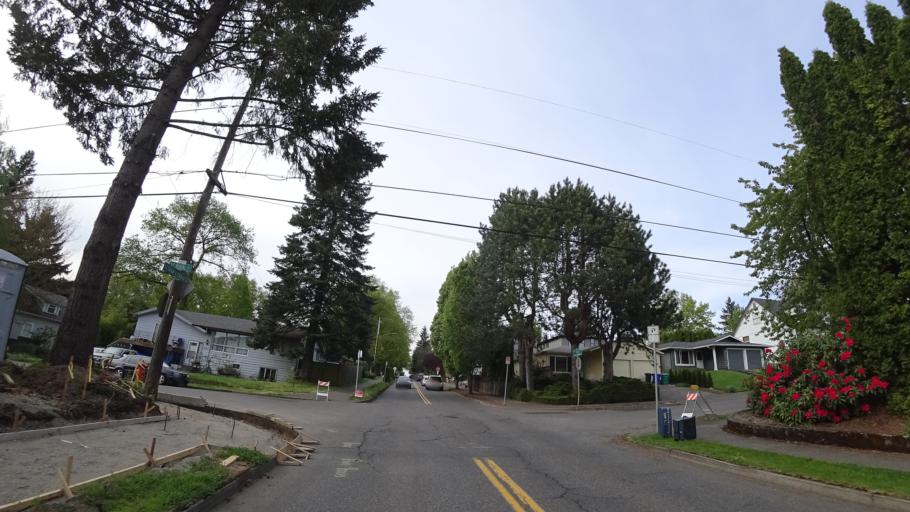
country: US
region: Oregon
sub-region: Clackamas County
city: Milwaukie
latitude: 45.4717
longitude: -122.6226
